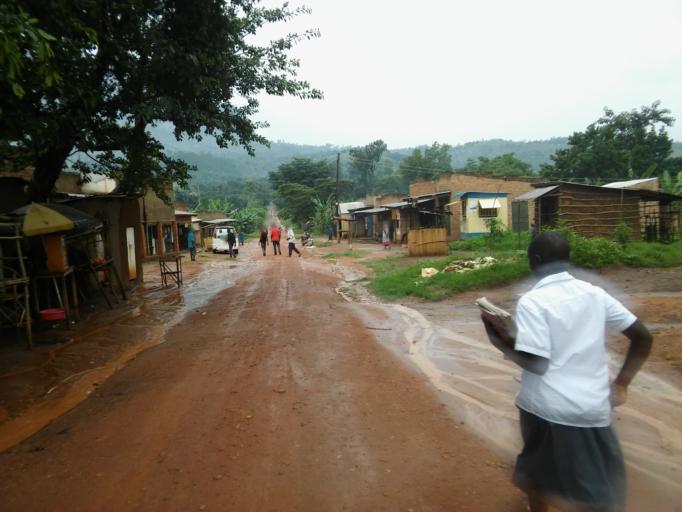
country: UG
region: Eastern Region
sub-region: Bududa District
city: Bududa
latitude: 0.9892
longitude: 34.2290
